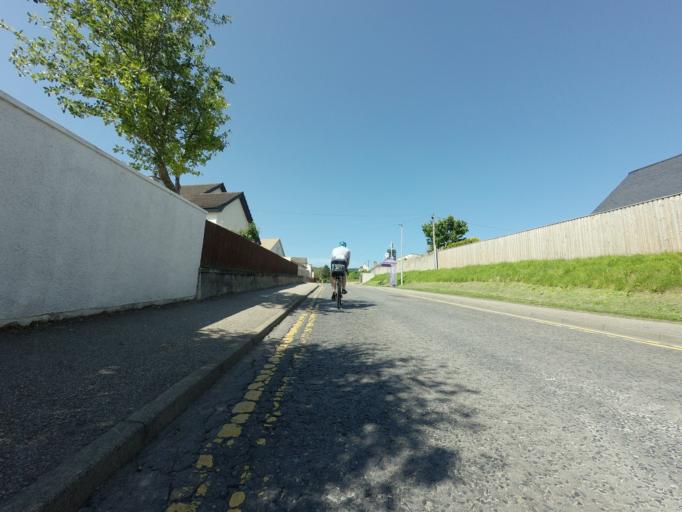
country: GB
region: Scotland
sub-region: Highland
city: Dingwall
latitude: 57.6024
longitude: -4.4295
